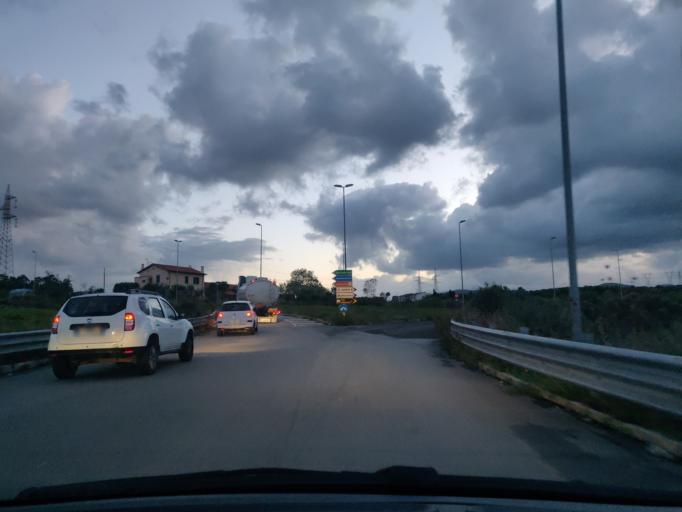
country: IT
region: Latium
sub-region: Citta metropolitana di Roma Capitale
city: Aurelia
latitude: 42.1318
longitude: 11.7753
